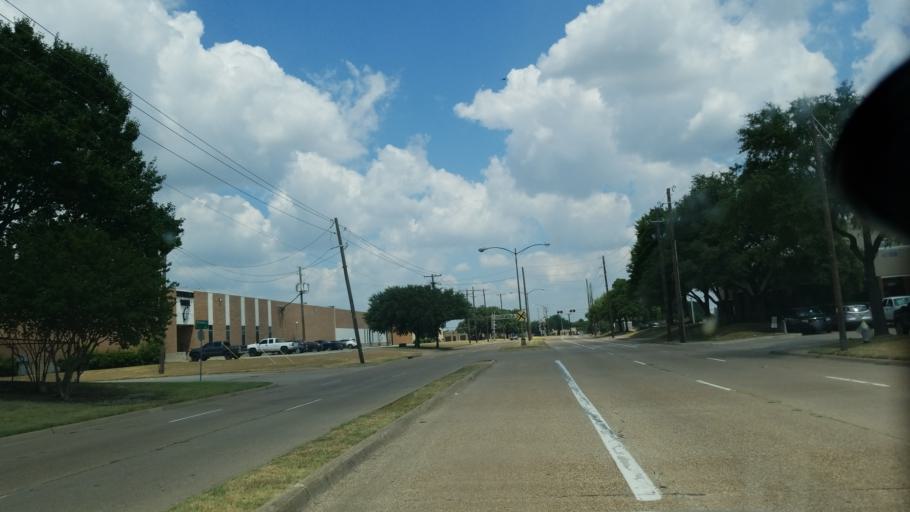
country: US
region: Texas
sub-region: Dallas County
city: Duncanville
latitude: 32.6848
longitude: -96.8828
